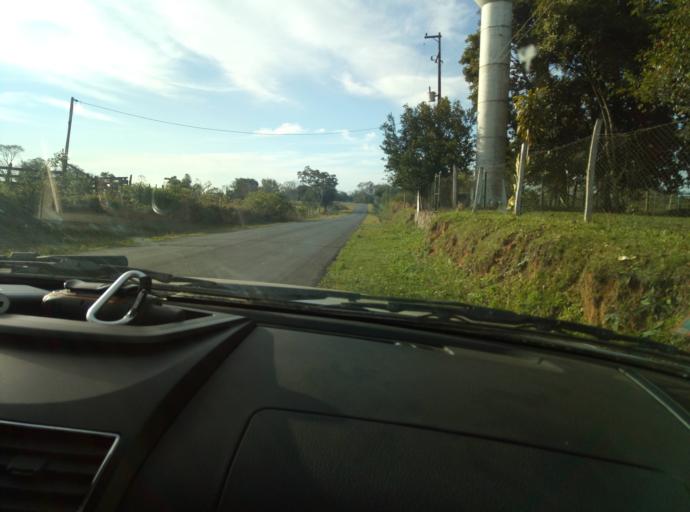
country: PY
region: Caaguazu
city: Carayao
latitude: -25.1588
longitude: -56.3119
